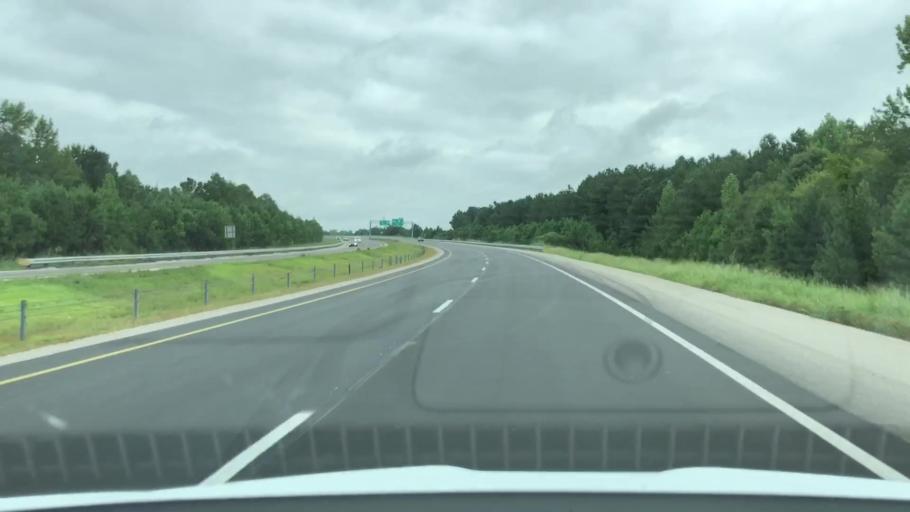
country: US
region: North Carolina
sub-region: Wilson County
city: Lucama
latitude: 35.6608
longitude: -77.9558
